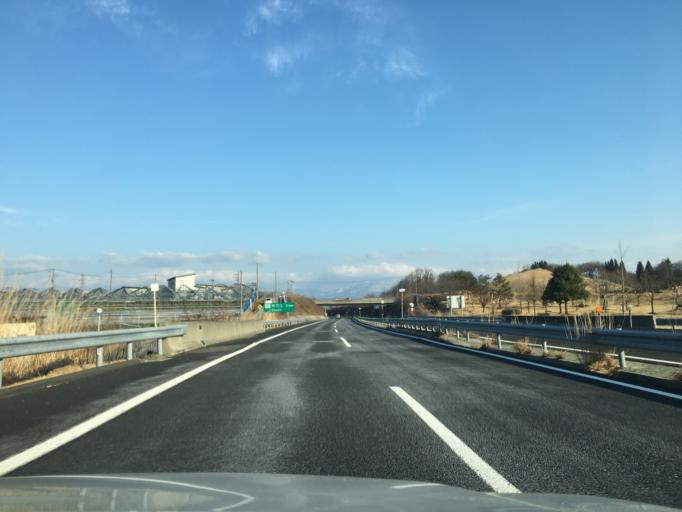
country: JP
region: Yamagata
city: Sagae
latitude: 38.3656
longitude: 140.2649
